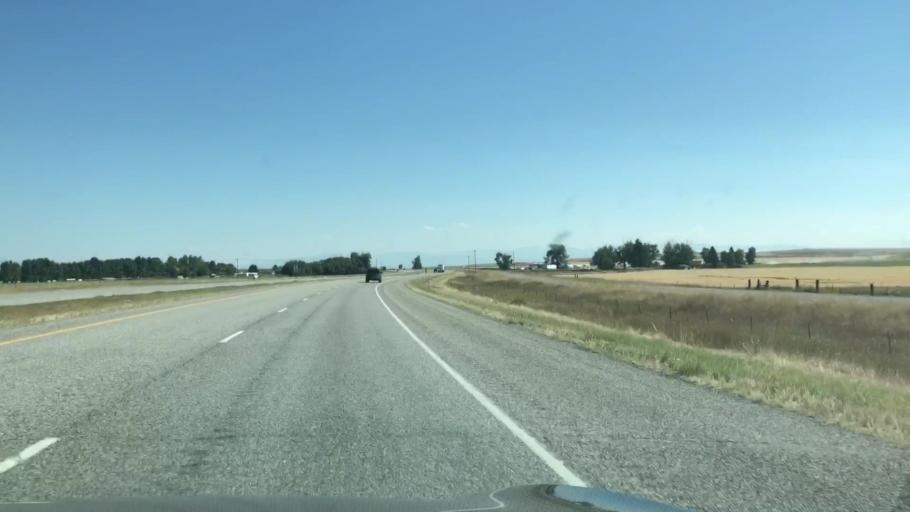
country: US
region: Montana
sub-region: Gallatin County
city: Manhattan
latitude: 45.8577
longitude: -111.3503
